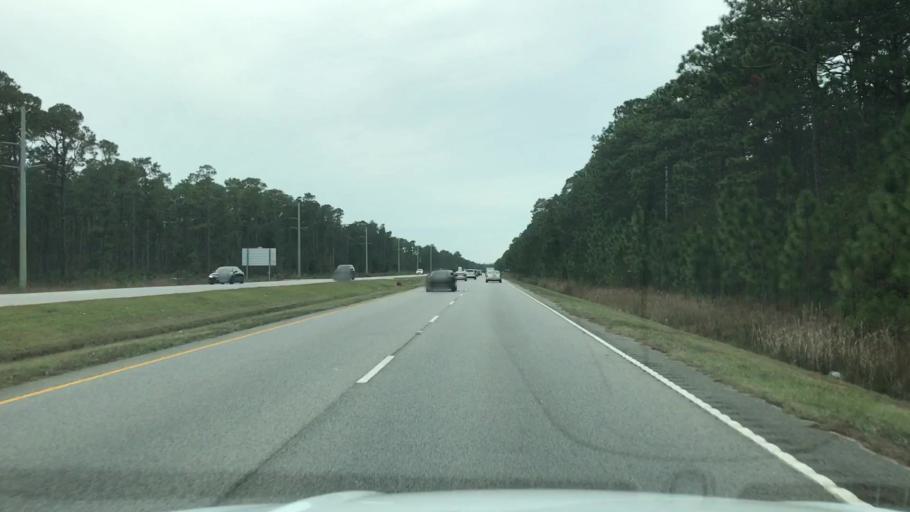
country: US
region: South Carolina
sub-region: Georgetown County
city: Georgetown
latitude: 33.4167
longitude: -79.1828
